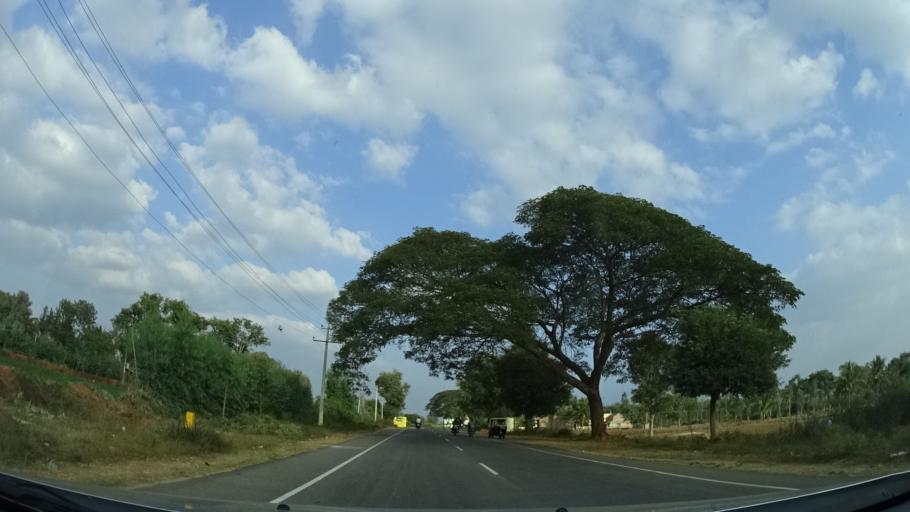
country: IN
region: Karnataka
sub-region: Mandya
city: Malavalli
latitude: 12.3612
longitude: 76.9864
